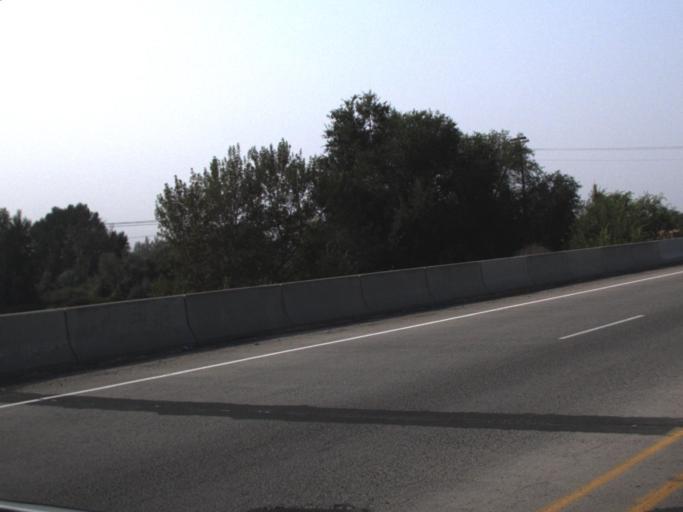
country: US
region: Washington
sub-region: Yakima County
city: Toppenish
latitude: 46.4134
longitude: -120.3142
